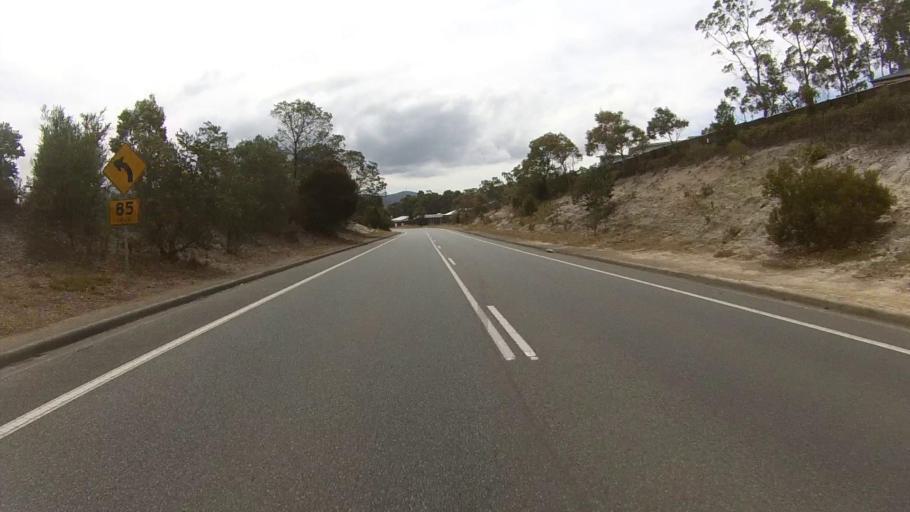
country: AU
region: Tasmania
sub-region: Kingborough
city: Kingston
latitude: -42.9915
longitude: 147.2943
